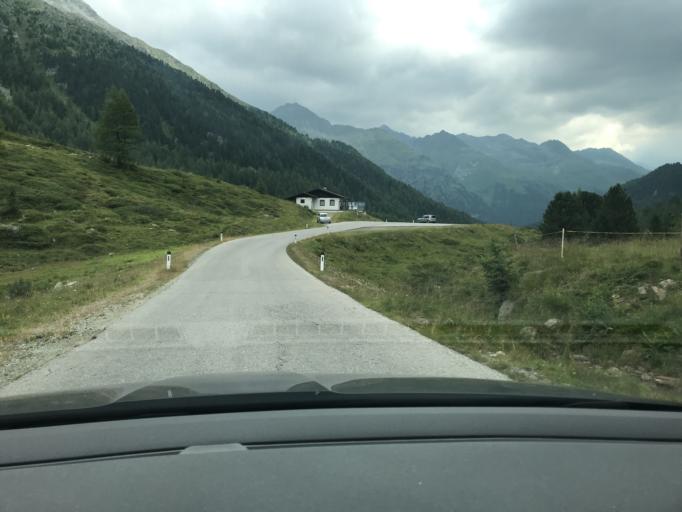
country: IT
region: Trentino-Alto Adige
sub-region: Bolzano
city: San Martino
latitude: 46.8966
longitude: 12.2175
